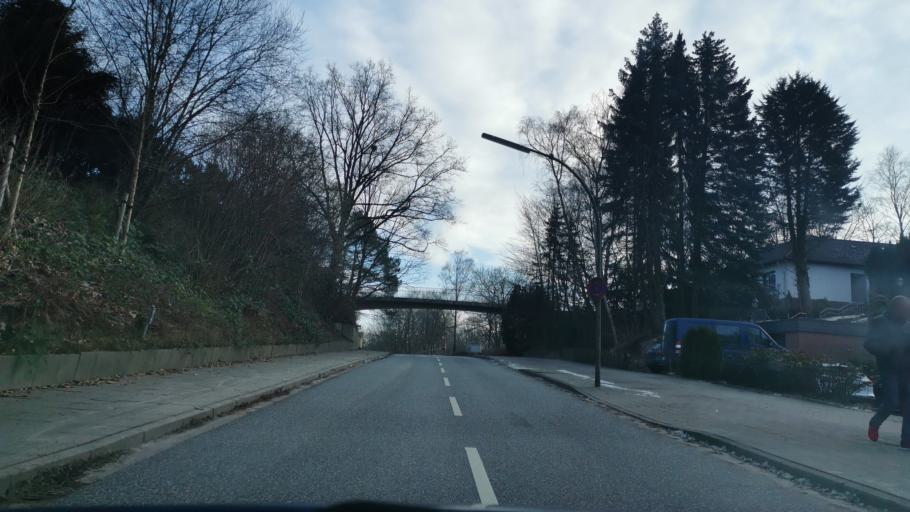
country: DE
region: Hamburg
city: Harburg
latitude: 53.4319
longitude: 9.9699
